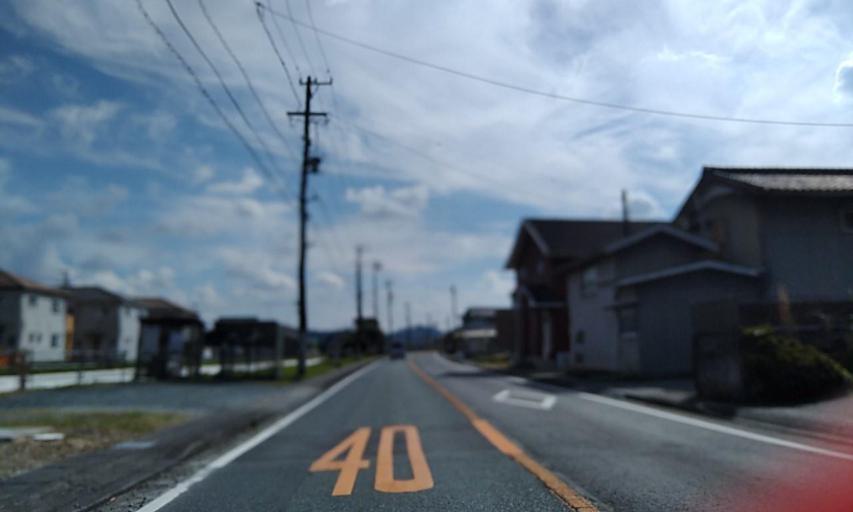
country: JP
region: Shizuoka
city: Hamakita
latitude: 34.8431
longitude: 137.8360
